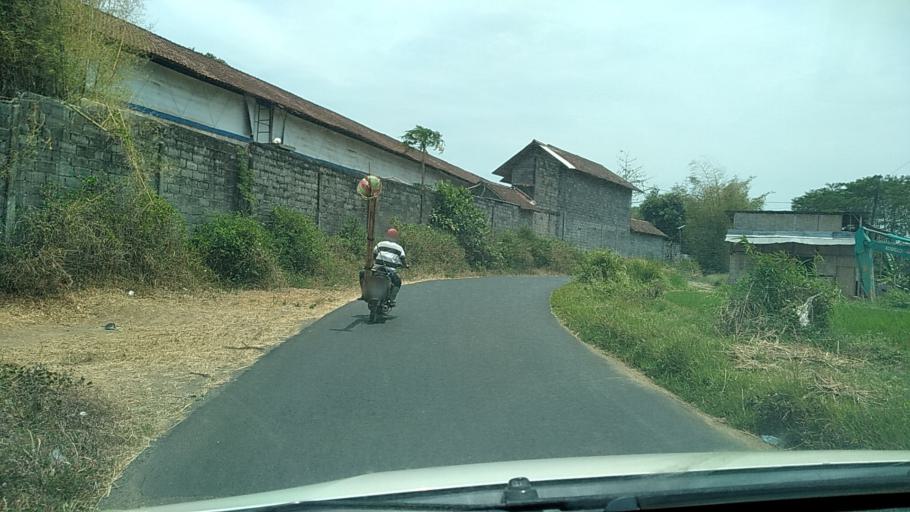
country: ID
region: Central Java
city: Ungaran
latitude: -7.1063
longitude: 110.3176
